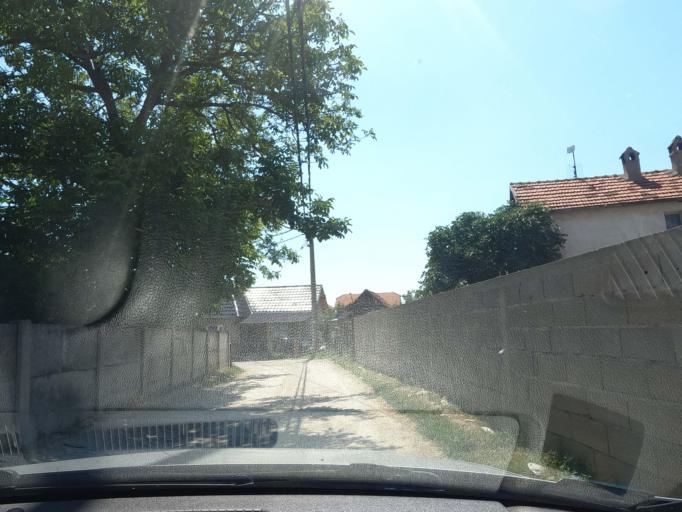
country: RS
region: Central Serbia
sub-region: Branicevski Okrug
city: Pozarevac
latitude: 44.7045
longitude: 21.1649
